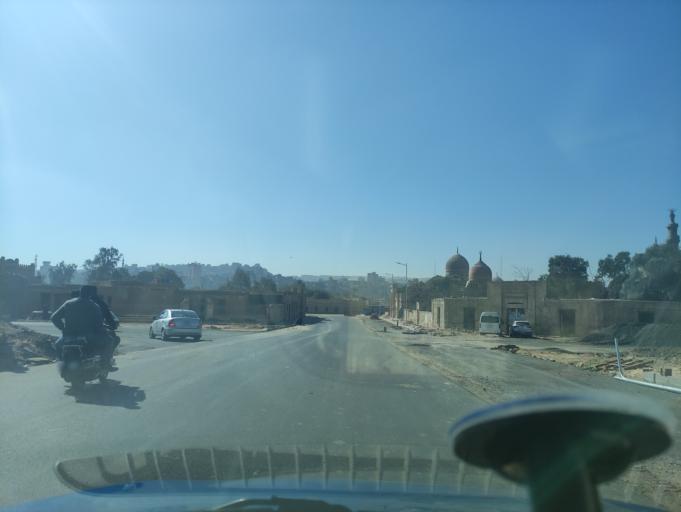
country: EG
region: Muhafazat al Qahirah
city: Cairo
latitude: 30.0541
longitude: 31.2801
